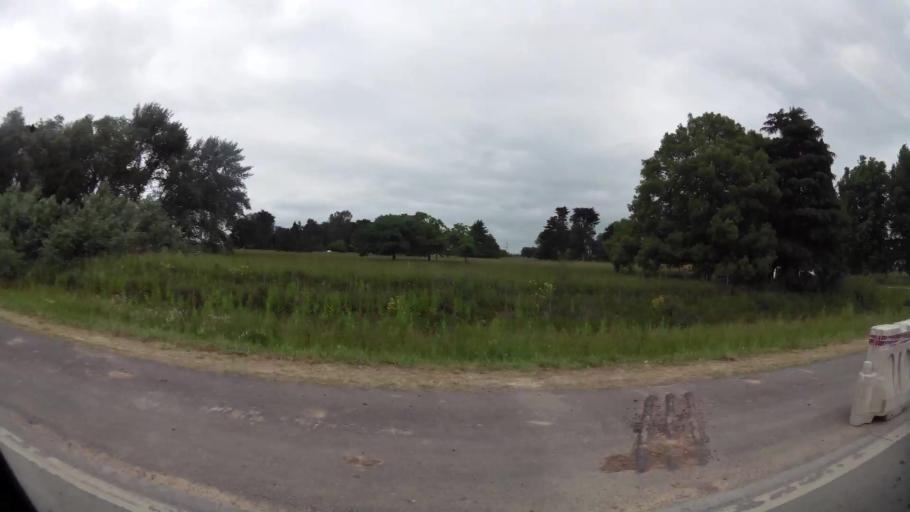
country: AR
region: Buenos Aires
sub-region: Partido de San Vicente
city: San Vicente
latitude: -35.0235
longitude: -58.3314
